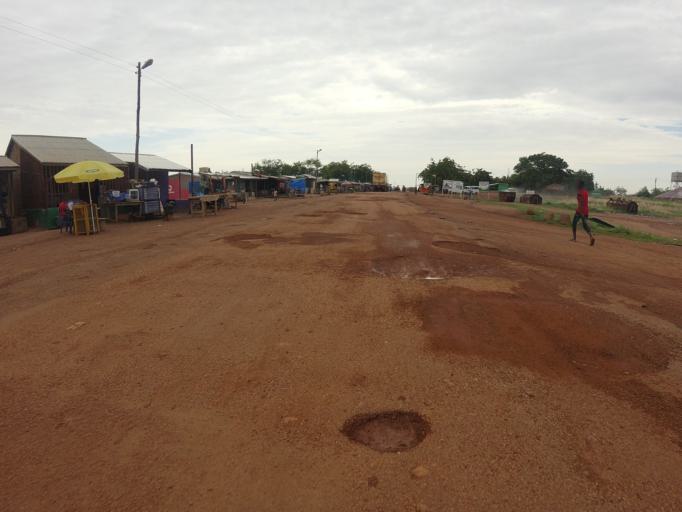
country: GH
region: Upper East
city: Bawku
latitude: 10.9347
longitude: -0.4984
